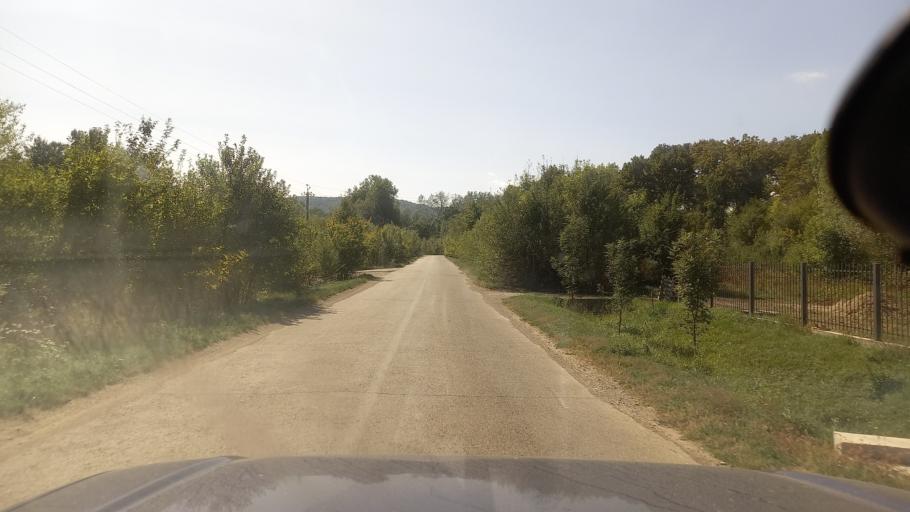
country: RU
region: Krasnodarskiy
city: Azovskaya
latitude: 44.7015
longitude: 38.6699
